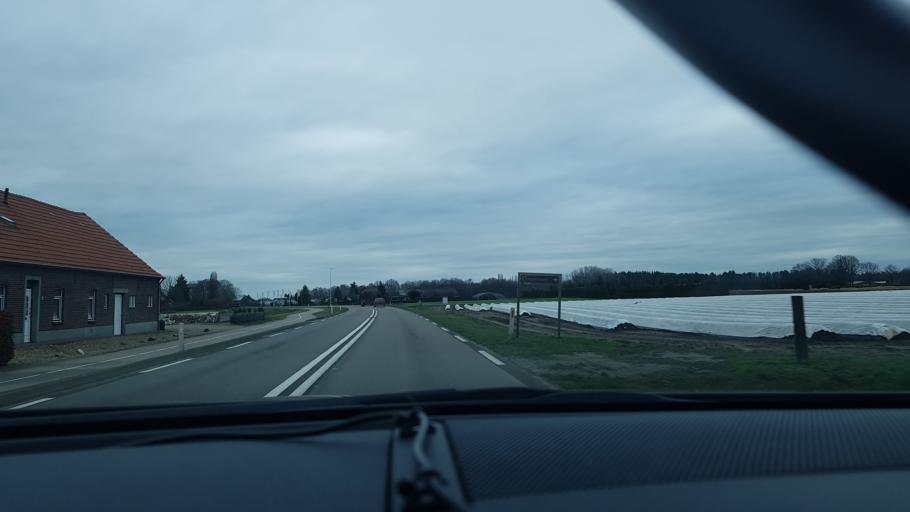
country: NL
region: Limburg
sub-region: Gemeente Leudal
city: Heythuysen
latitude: 51.2836
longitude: 5.9097
